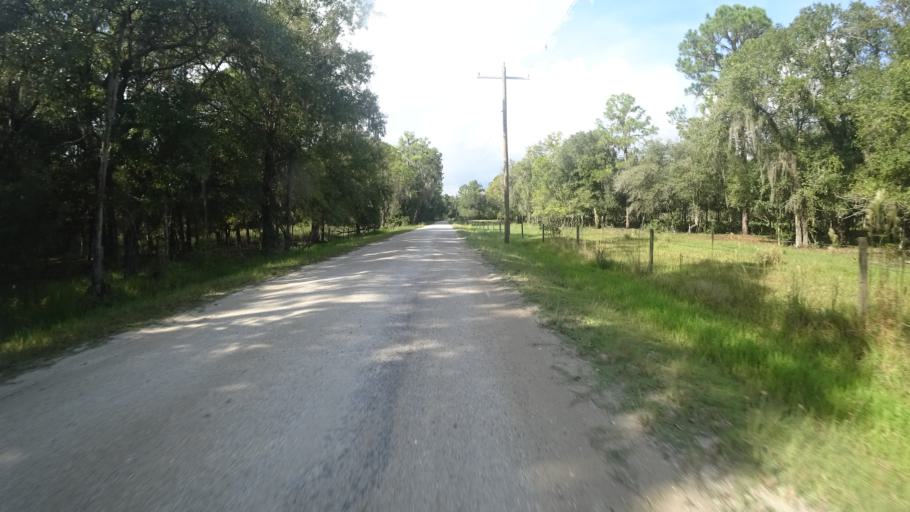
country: US
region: Florida
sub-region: Hillsborough County
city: Balm
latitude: 27.6287
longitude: -82.1233
